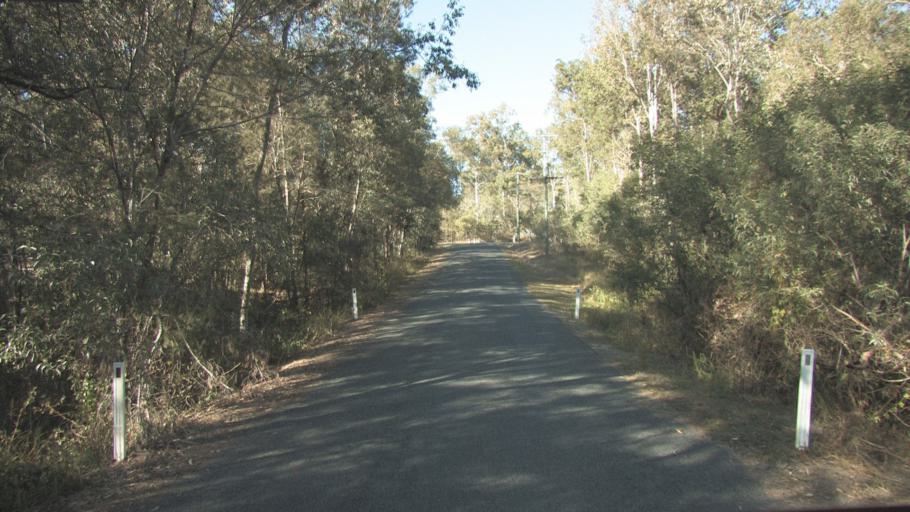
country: AU
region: Queensland
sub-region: Logan
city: North Maclean
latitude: -27.7828
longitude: 152.9653
